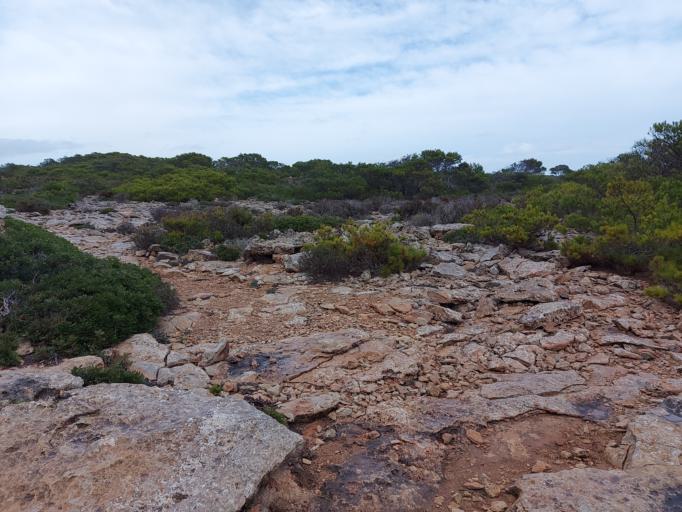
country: ES
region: Balearic Islands
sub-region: Illes Balears
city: Llucmajor
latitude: 39.3589
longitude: 2.8179
